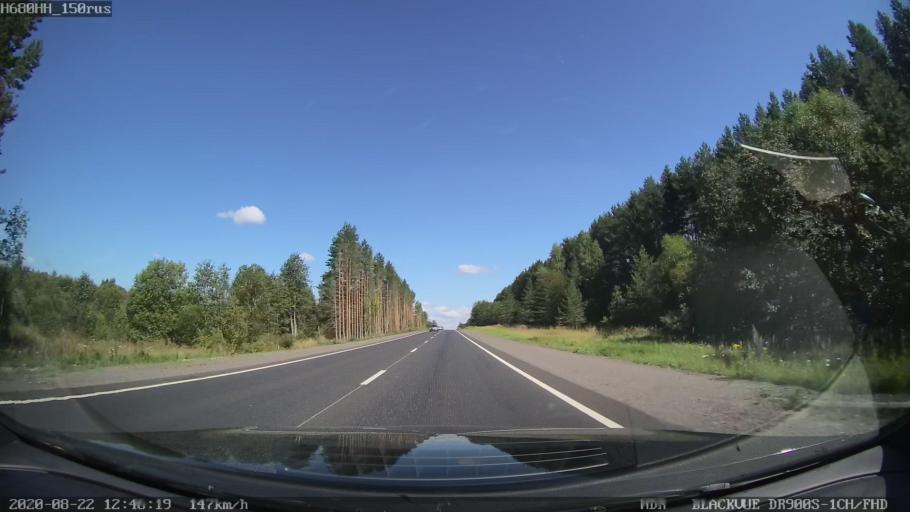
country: RU
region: Tverskaya
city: Rameshki
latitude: 57.4181
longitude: 36.1432
